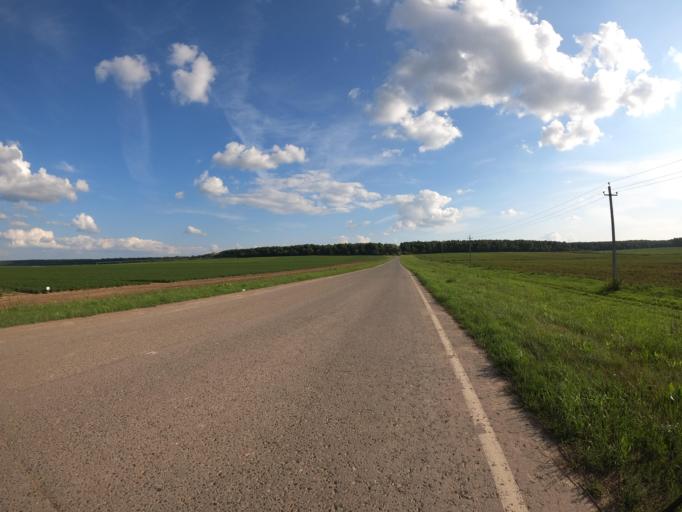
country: RU
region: Moskovskaya
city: Meshcherino
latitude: 55.1872
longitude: 38.4718
